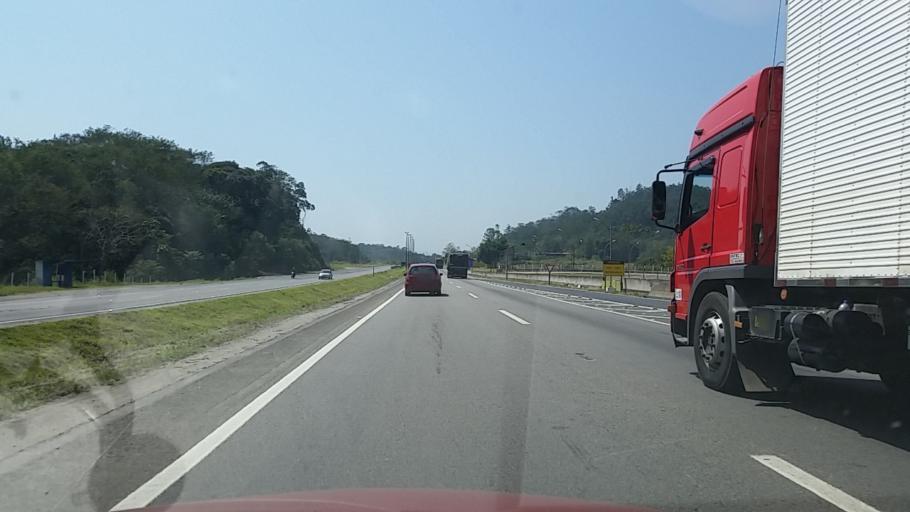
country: BR
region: Sao Paulo
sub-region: Miracatu
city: Miracatu
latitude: -24.2687
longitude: -47.3962
